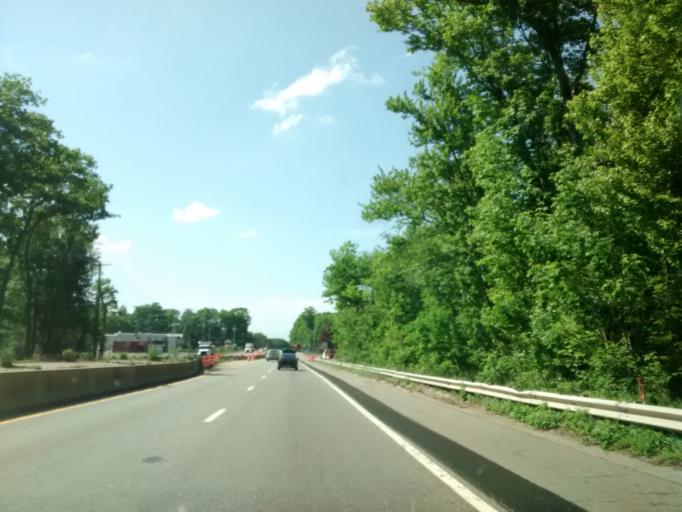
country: US
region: Massachusetts
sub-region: Worcester County
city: Millbury
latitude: 42.1750
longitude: -71.7554
